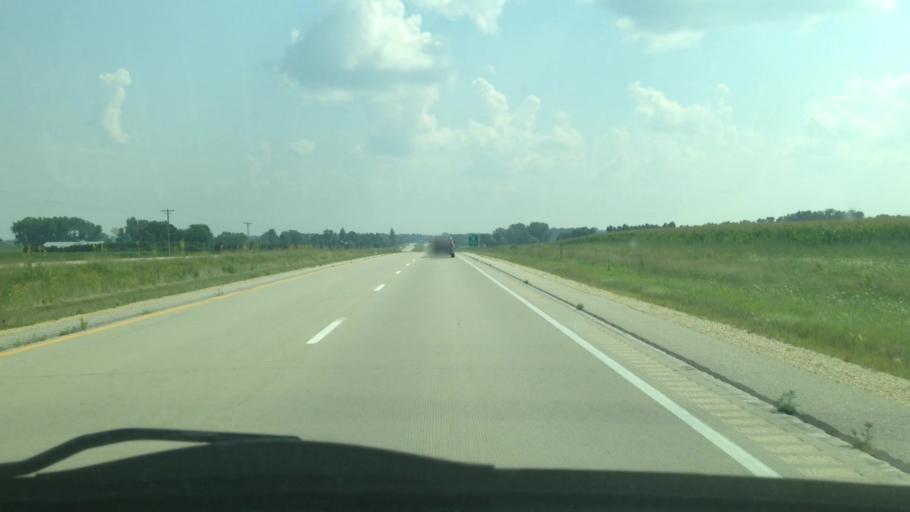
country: US
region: Iowa
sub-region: Bremer County
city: Denver
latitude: 42.7376
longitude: -92.3377
